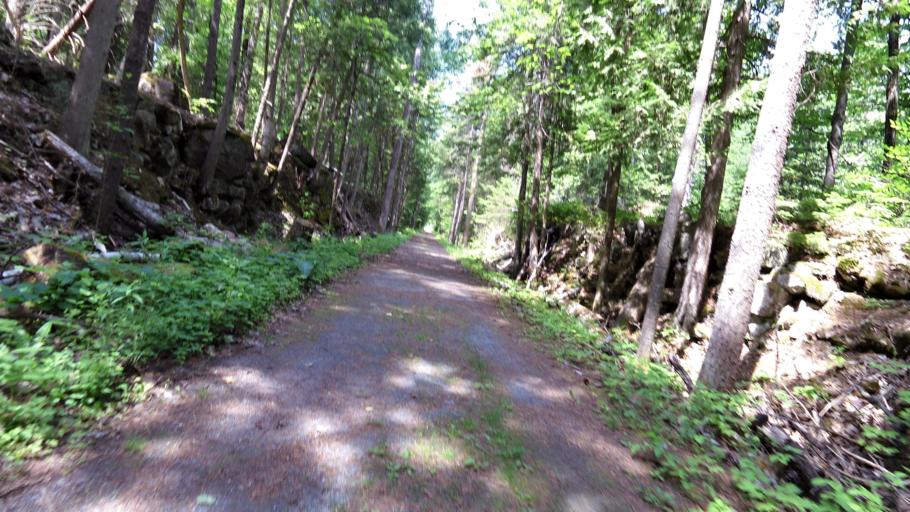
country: CA
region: Ontario
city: Arnprior
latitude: 45.4597
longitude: -76.2594
